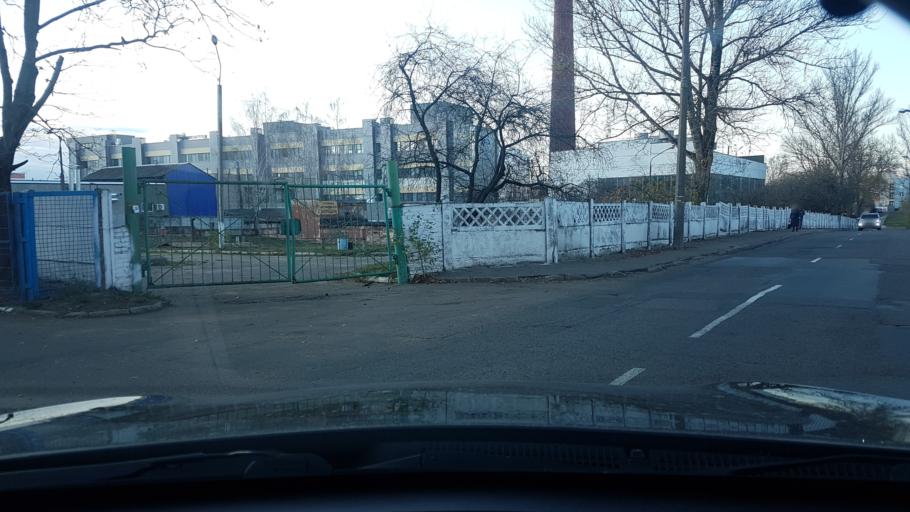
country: BY
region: Minsk
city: Minsk
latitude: 53.9344
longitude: 27.5419
